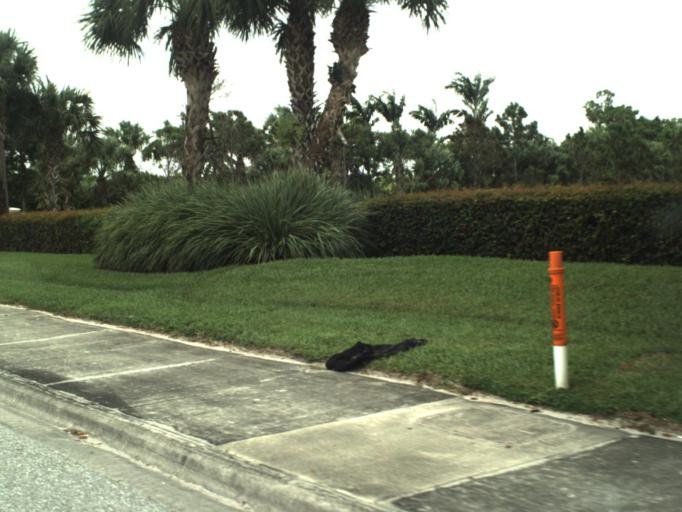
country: US
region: Florida
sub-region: Palm Beach County
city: Greenacres City
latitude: 26.6175
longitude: -80.1784
